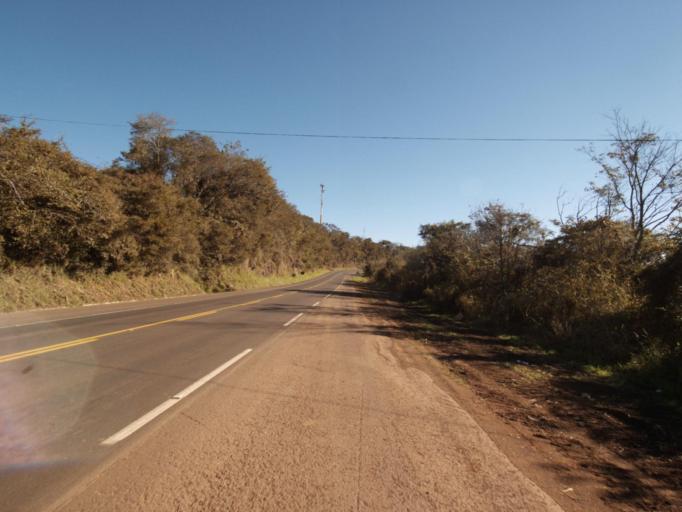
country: BR
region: Santa Catarina
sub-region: Chapeco
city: Chapeco
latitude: -26.9828
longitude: -52.5988
